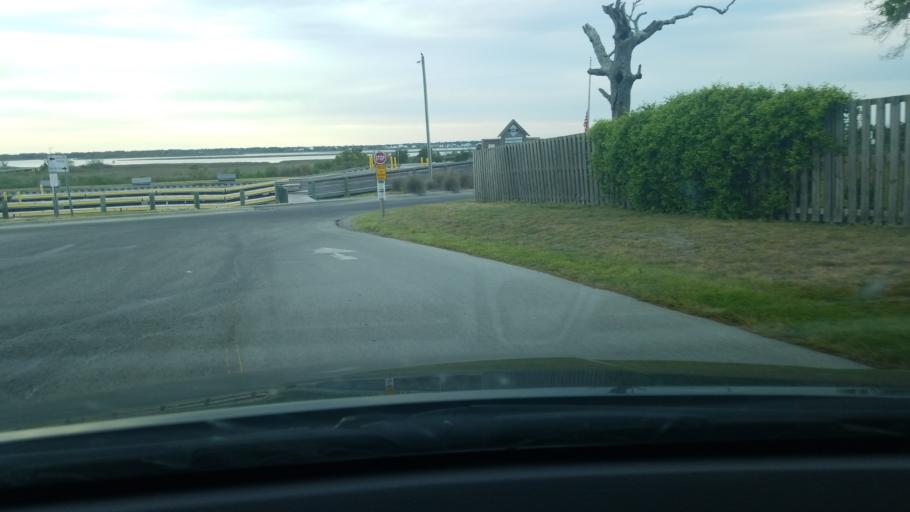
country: US
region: North Carolina
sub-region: Carteret County
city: Emerald Isle
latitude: 34.6708
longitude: -77.0060
